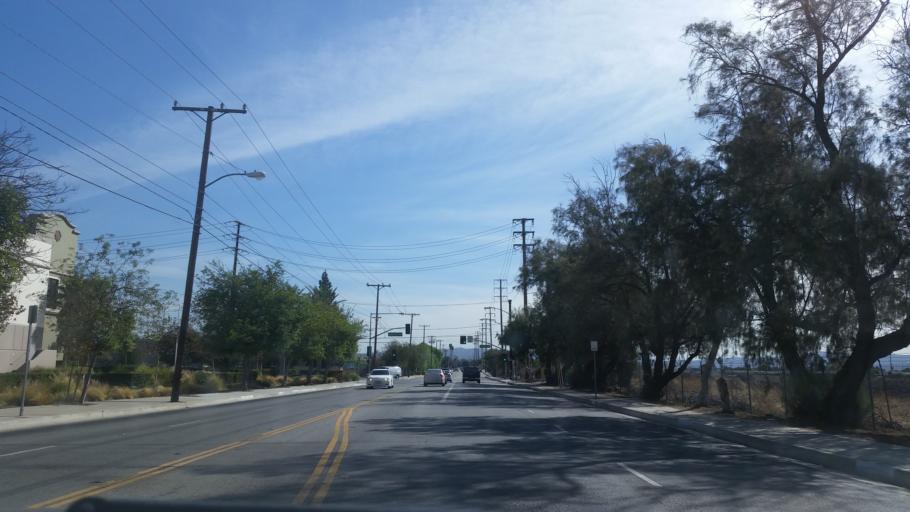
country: US
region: California
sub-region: Los Angeles County
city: Irwindale
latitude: 34.0973
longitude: -117.9430
